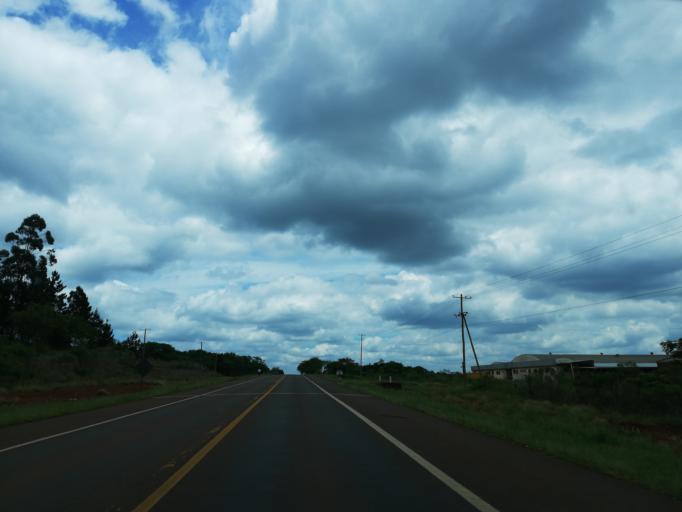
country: AR
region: Misiones
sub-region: Departamento de Leandro N. Alem
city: Leandro N. Alem
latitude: -27.6315
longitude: -55.3419
